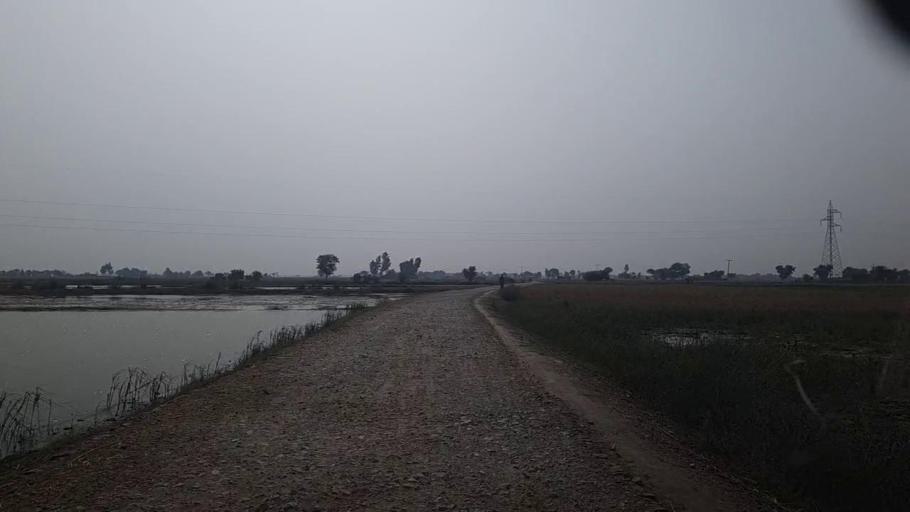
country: PK
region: Sindh
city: Kashmor
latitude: 28.3943
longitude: 69.4218
